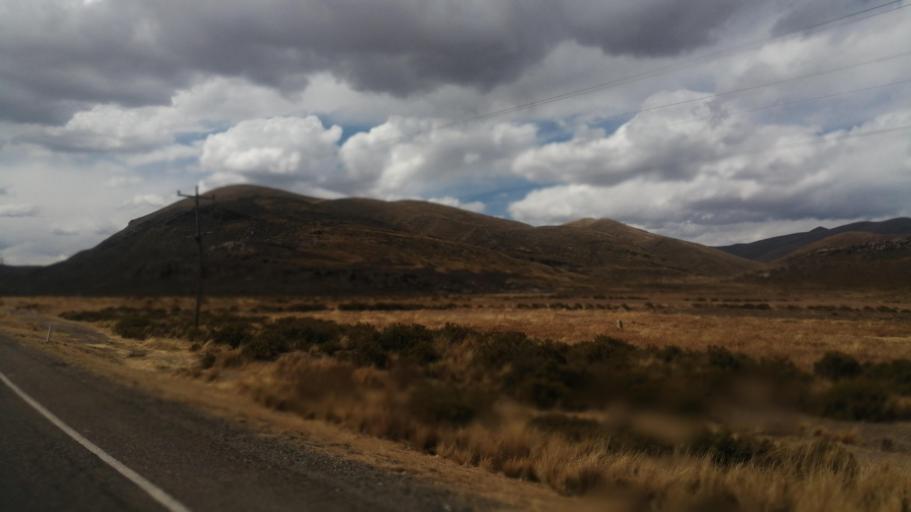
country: BO
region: Oruro
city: Challapata
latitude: -18.7544
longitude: -66.8623
